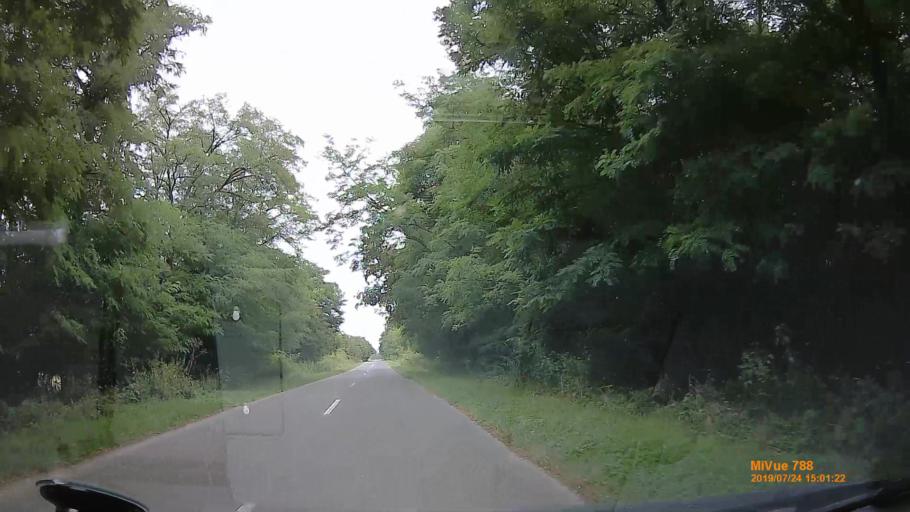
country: HU
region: Szabolcs-Szatmar-Bereg
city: Vasarosnameny
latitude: 48.2288
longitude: 22.3876
